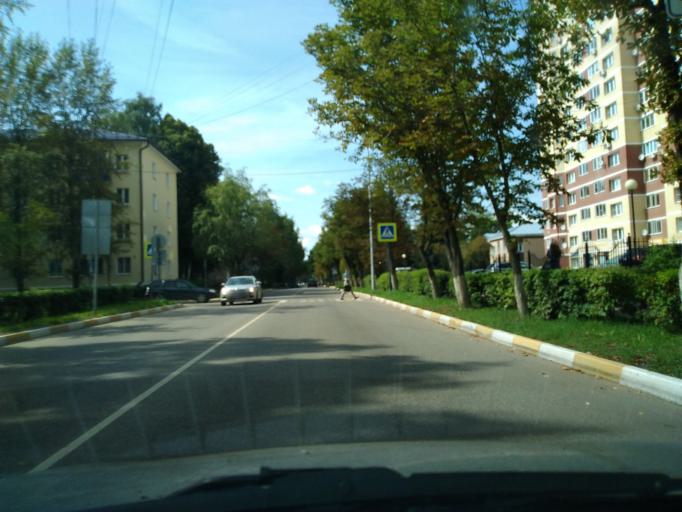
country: RU
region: Moskovskaya
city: Voskresensk
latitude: 55.3253
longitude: 38.6667
